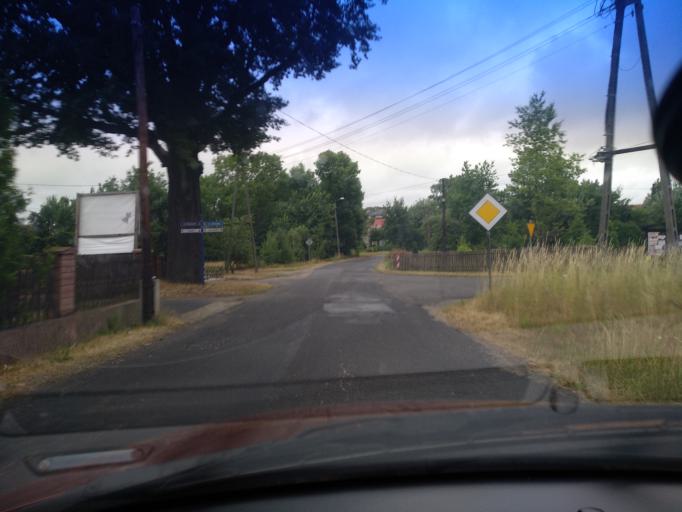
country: PL
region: Lower Silesian Voivodeship
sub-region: Powiat zgorzelecki
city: Wegliniec
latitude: 51.2472
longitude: 15.2155
